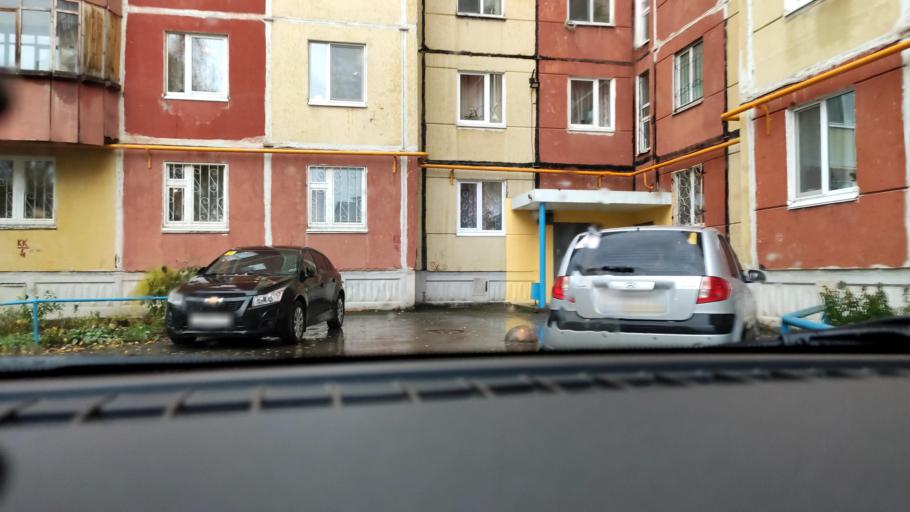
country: RU
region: Perm
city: Perm
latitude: 58.0199
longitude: 56.3009
